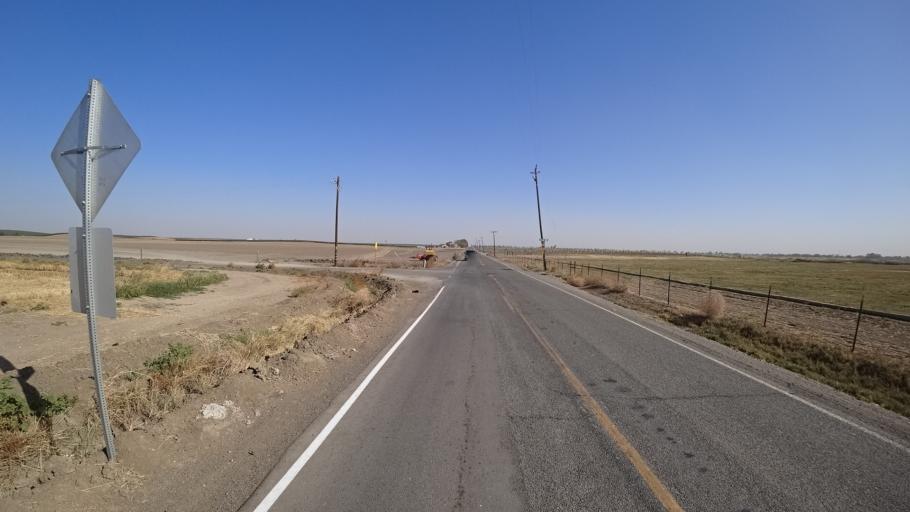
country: US
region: California
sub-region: Yolo County
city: Cottonwood
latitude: 38.7144
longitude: -121.9227
